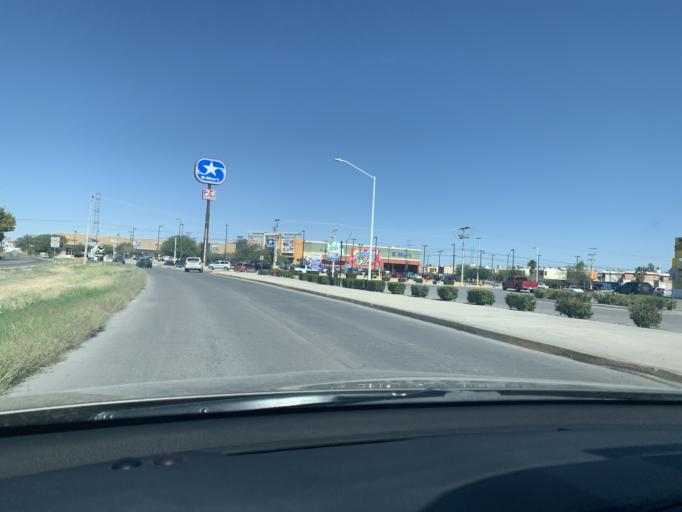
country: US
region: Texas
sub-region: El Paso County
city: Socorro
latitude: 31.6945
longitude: -106.3812
